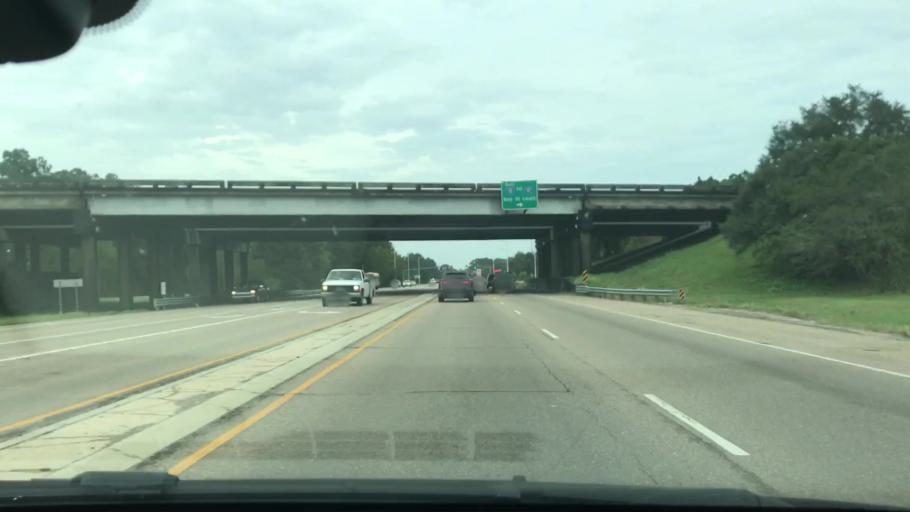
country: US
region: Louisiana
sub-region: Saint Tammany Parish
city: Slidell
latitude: 30.3111
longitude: -89.7704
